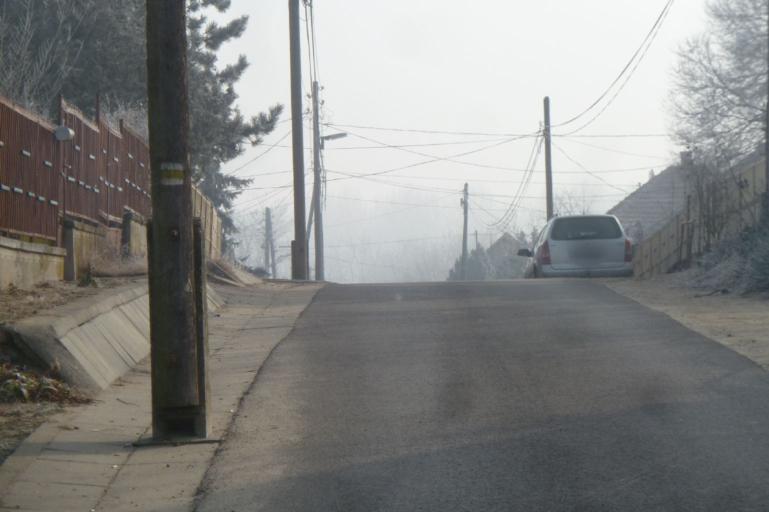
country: HU
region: Pest
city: Ujszilvas
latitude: 47.2714
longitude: 19.9127
